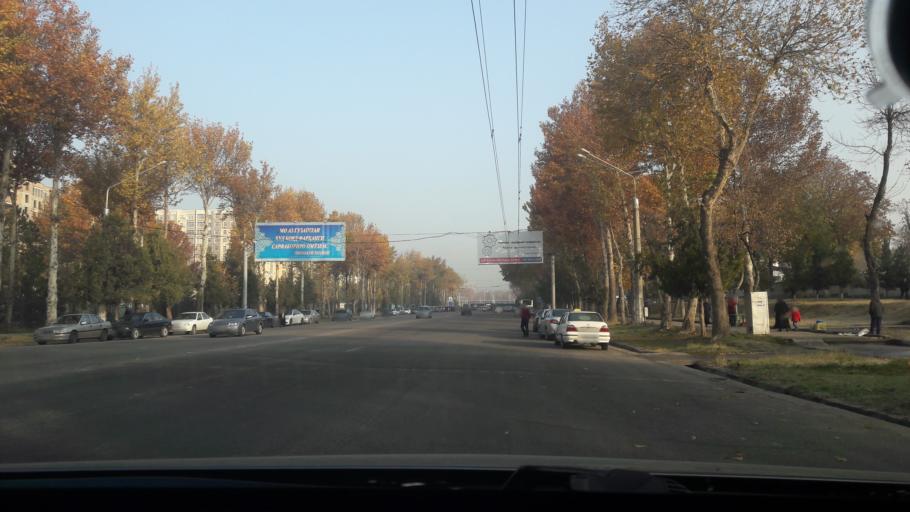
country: TJ
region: Dushanbe
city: Dushanbe
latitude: 38.5781
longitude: 68.7550
